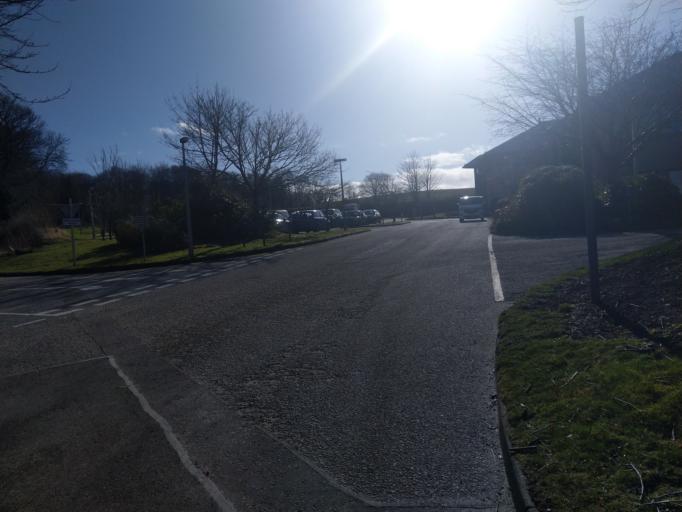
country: GB
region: Scotland
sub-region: Aberdeen City
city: Dyce
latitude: 57.1851
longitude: -2.2119
